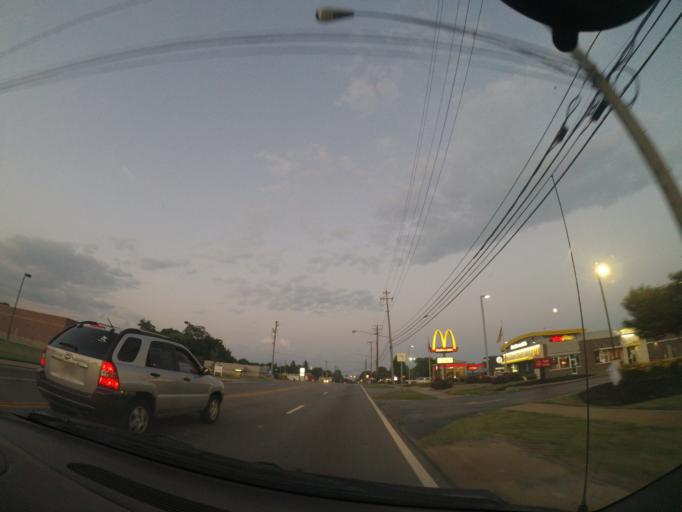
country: US
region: Ohio
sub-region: Lake County
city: North Madison
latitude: 41.8024
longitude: -81.0516
